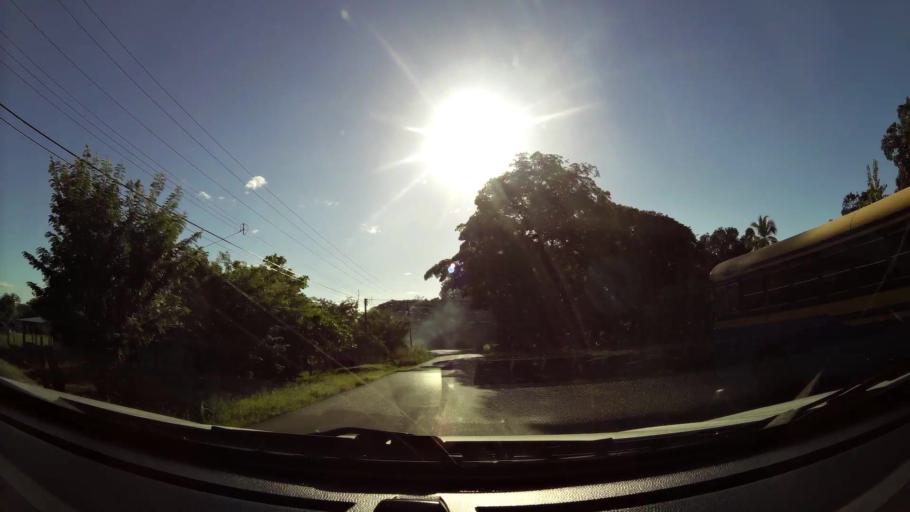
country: CR
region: Guanacaste
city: Sardinal
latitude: 10.4914
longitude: -85.6322
